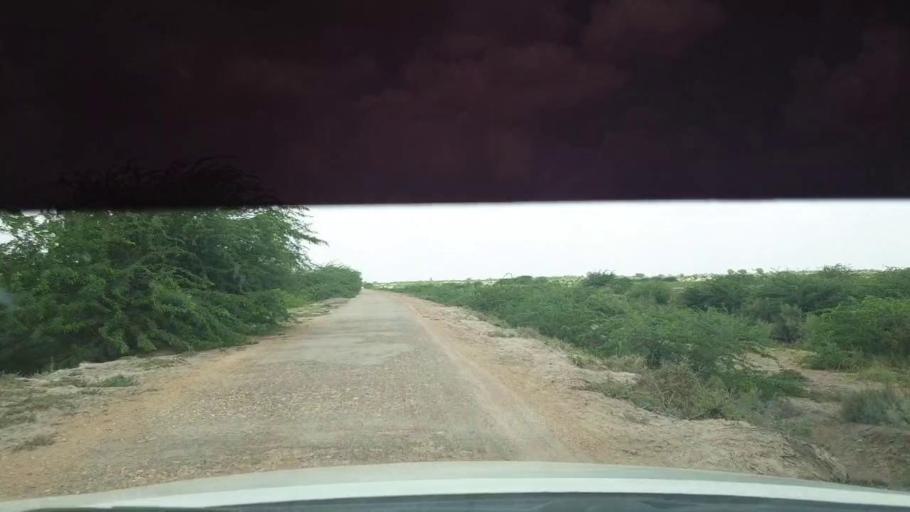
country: PK
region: Sindh
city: Kadhan
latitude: 24.4798
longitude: 69.0660
